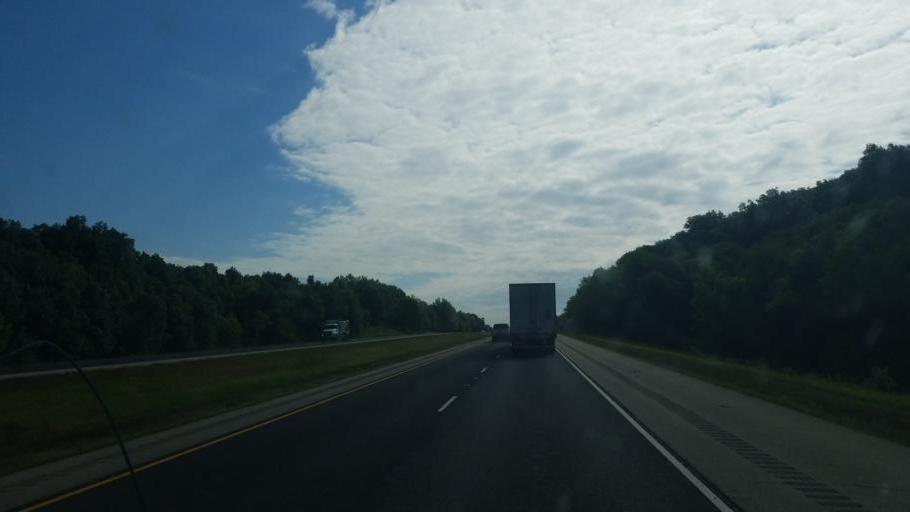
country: US
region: Illinois
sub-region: Clark County
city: Marshall
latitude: 39.3956
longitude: -87.7851
